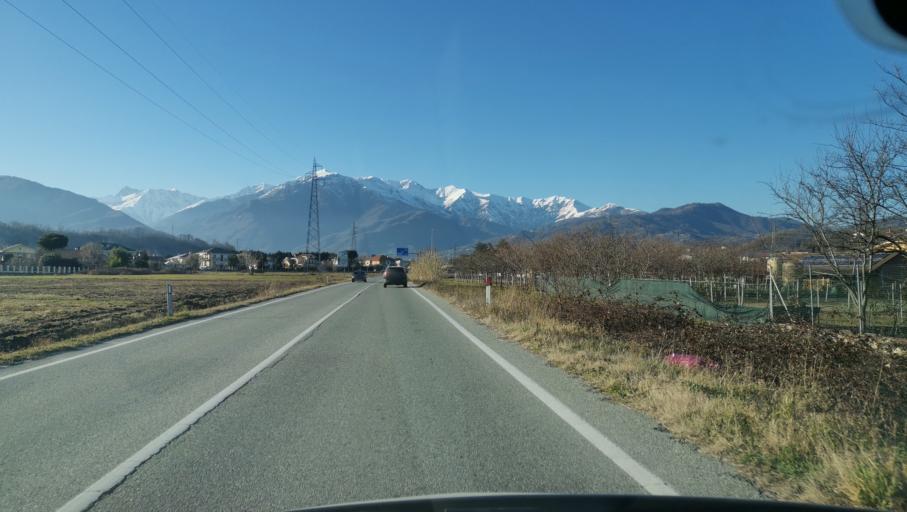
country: IT
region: Piedmont
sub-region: Provincia di Torino
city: Bibiana
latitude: 44.8046
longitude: 7.2919
